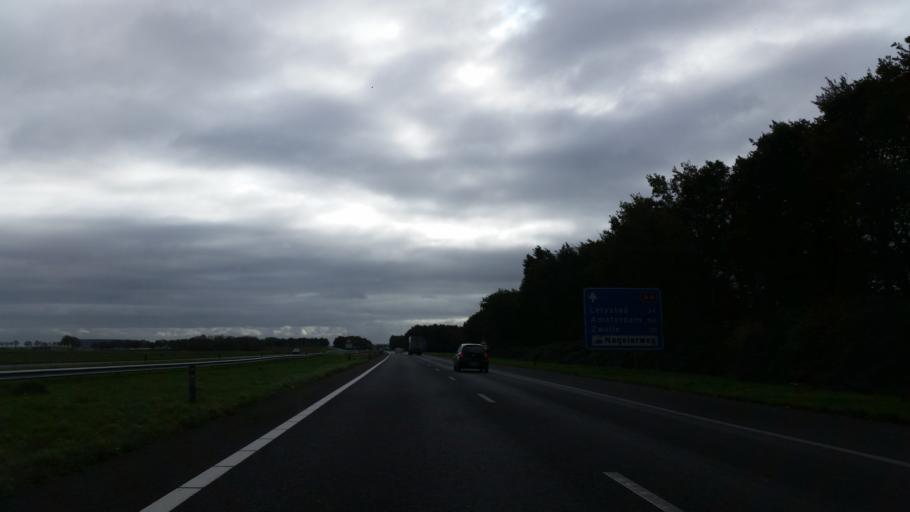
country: NL
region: Flevoland
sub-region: Gemeente Noordoostpolder
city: Emmeloord
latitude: 52.7360
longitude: 5.7690
